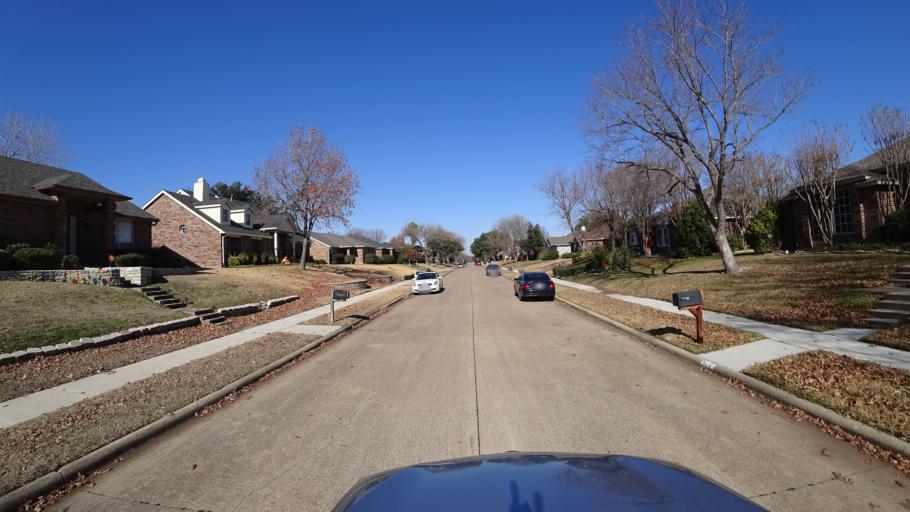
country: US
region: Texas
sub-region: Denton County
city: Lewisville
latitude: 33.0097
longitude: -97.0158
